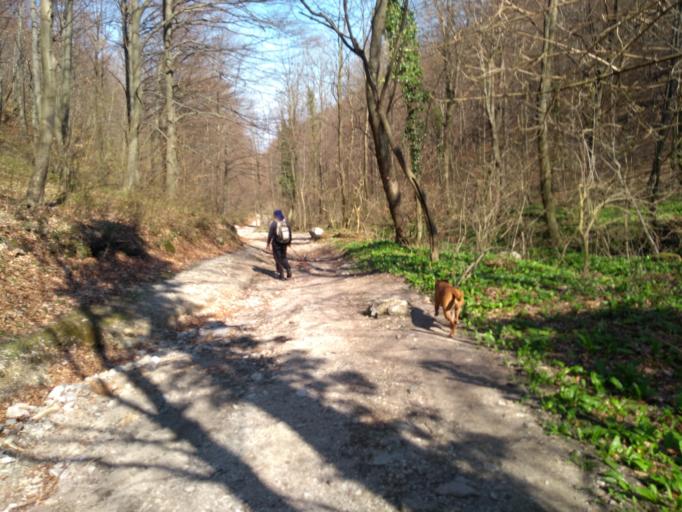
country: HR
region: Varazdinska
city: Ivanec
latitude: 46.1911
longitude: 16.1176
